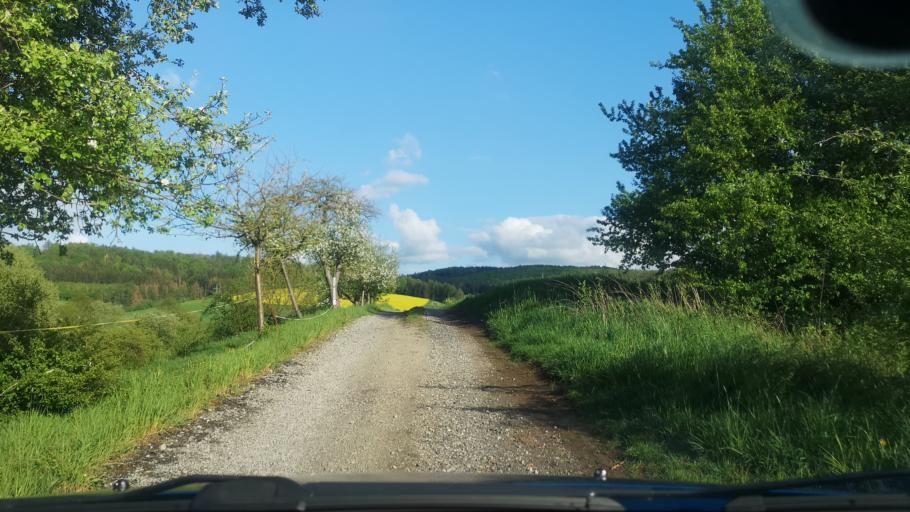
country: DE
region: Lower Saxony
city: Uslar
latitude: 51.6480
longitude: 9.6786
